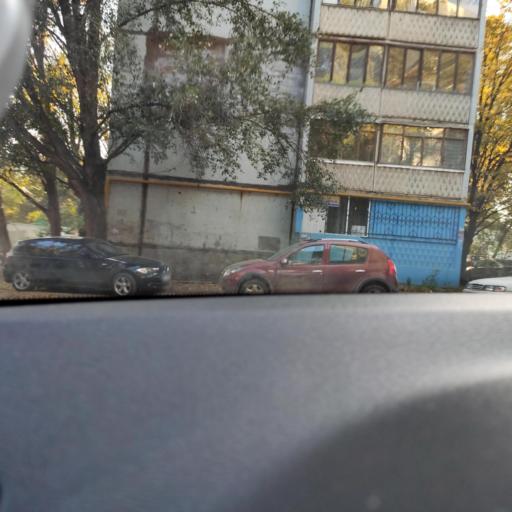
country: RU
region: Samara
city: Samara
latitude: 53.2441
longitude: 50.2335
